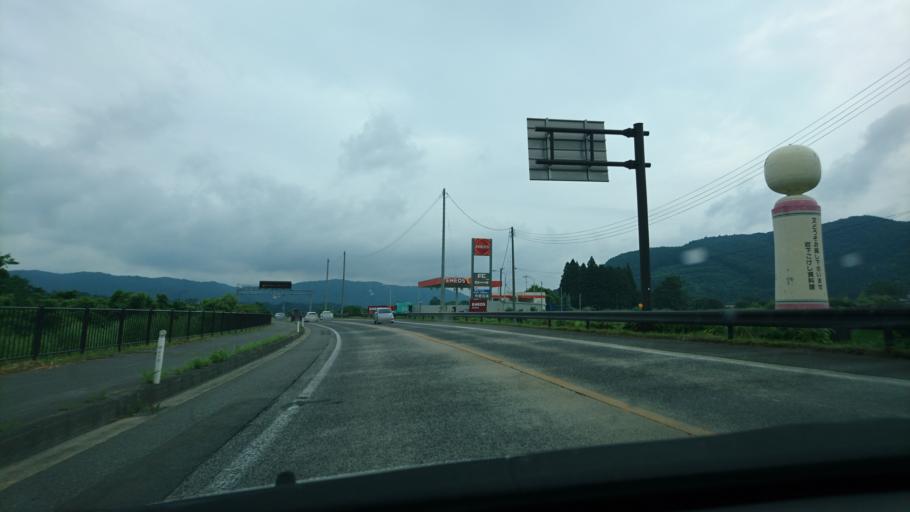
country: JP
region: Miyagi
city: Furukawa
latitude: 38.7331
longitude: 140.7569
